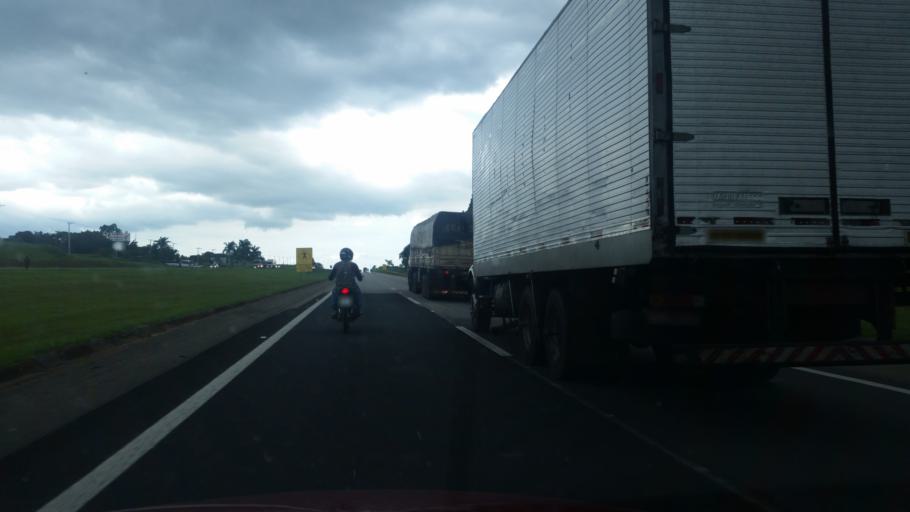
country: BR
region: Sao Paulo
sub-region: Porto Feliz
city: Porto Feliz
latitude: -23.3348
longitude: -47.5499
